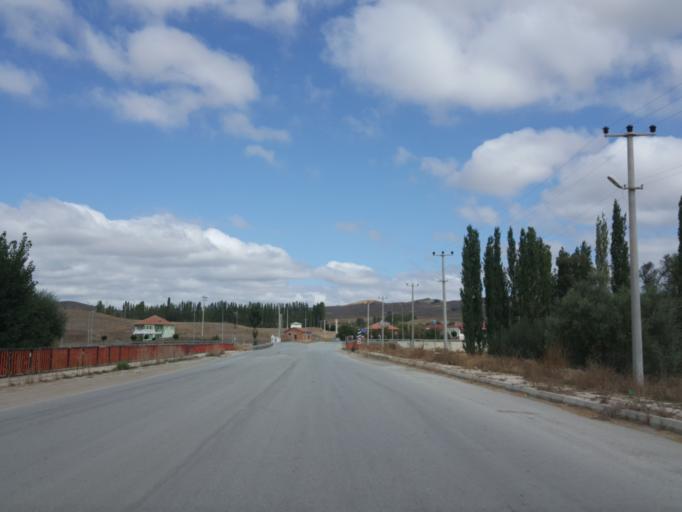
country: TR
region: Sivas
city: Yavu
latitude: 39.7956
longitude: 36.2035
